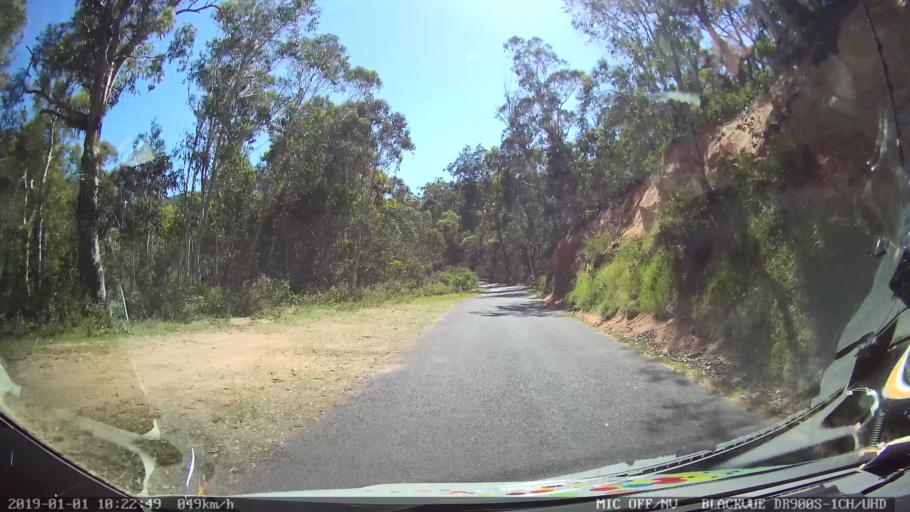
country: AU
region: New South Wales
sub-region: Snowy River
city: Jindabyne
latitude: -36.0771
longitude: 148.2073
